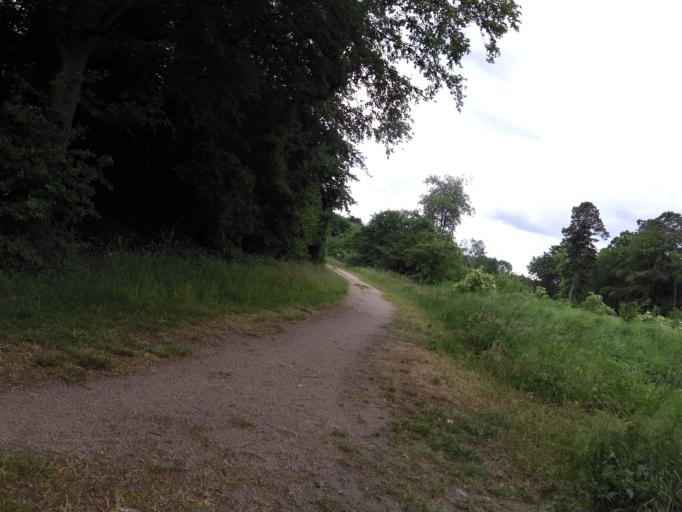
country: DE
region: Hesse
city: Morfelden-Walldorf
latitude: 50.0186
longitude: 8.5809
